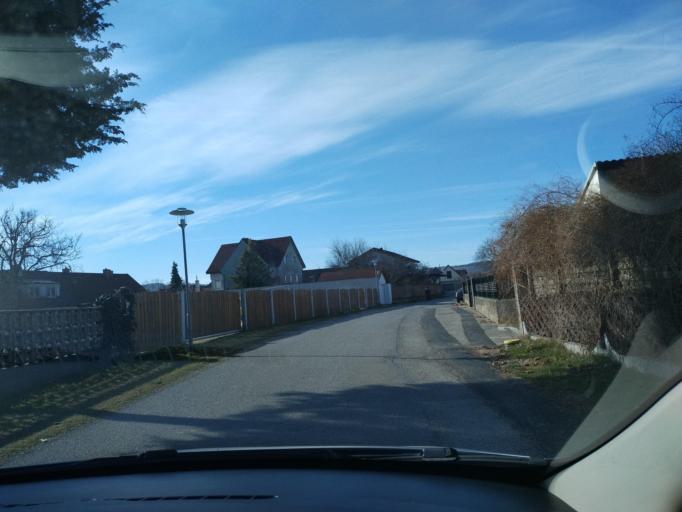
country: AT
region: Lower Austria
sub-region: Politischer Bezirk Wiener Neustadt
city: Lanzenkirchen
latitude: 47.7425
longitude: 16.2375
